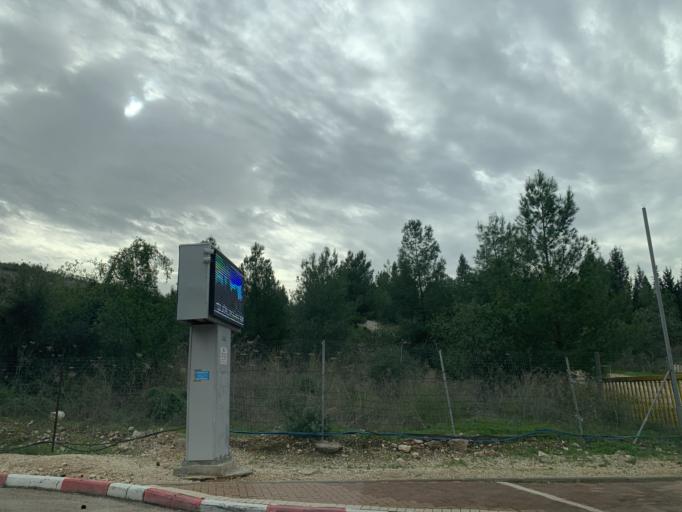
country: IL
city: Nirit
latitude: 32.1465
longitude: 34.9799
